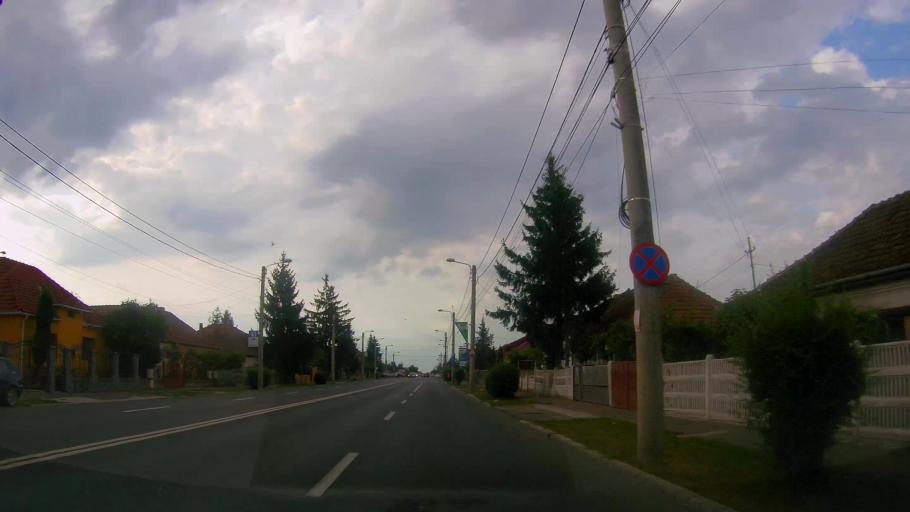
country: RO
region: Satu Mare
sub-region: Municipiul Satu Mare
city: Satu Mare
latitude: 47.7639
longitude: 22.8834
